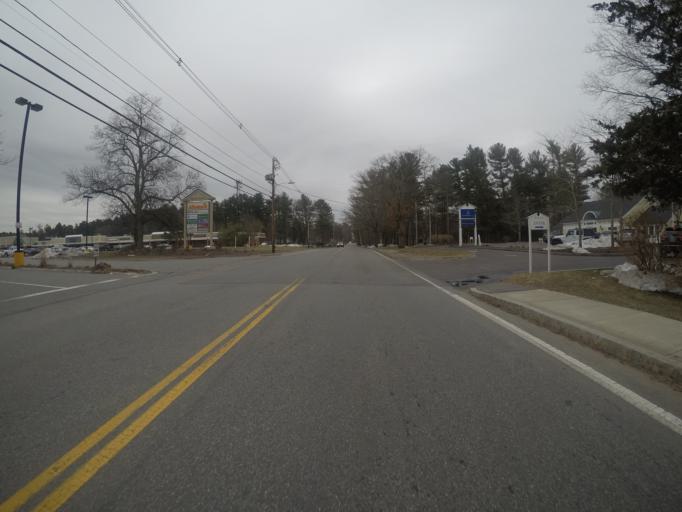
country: US
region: Massachusetts
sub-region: Bristol County
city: Easton
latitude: 42.0230
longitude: -71.1186
